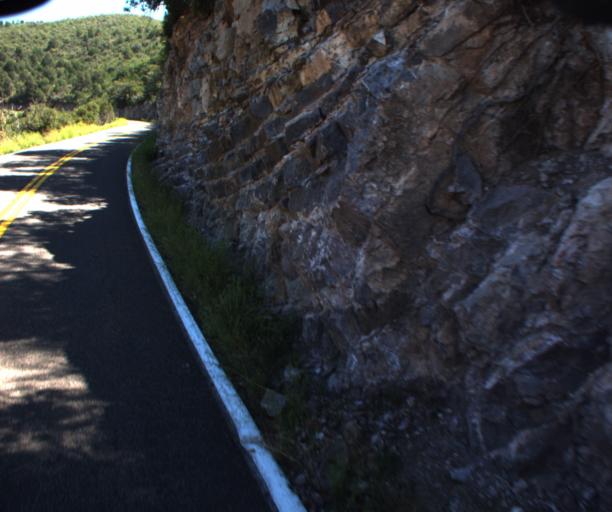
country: US
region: Arizona
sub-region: Greenlee County
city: Morenci
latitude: 33.1947
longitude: -109.3822
